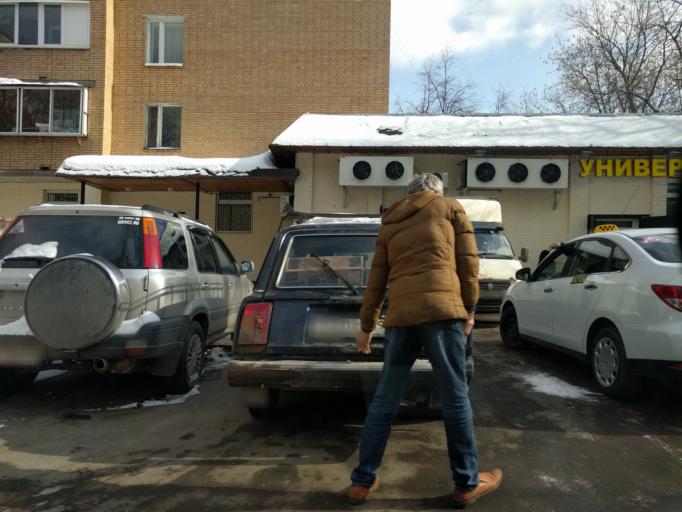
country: RU
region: Moskovskaya
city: Izmaylovo
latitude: 55.7909
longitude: 37.8058
